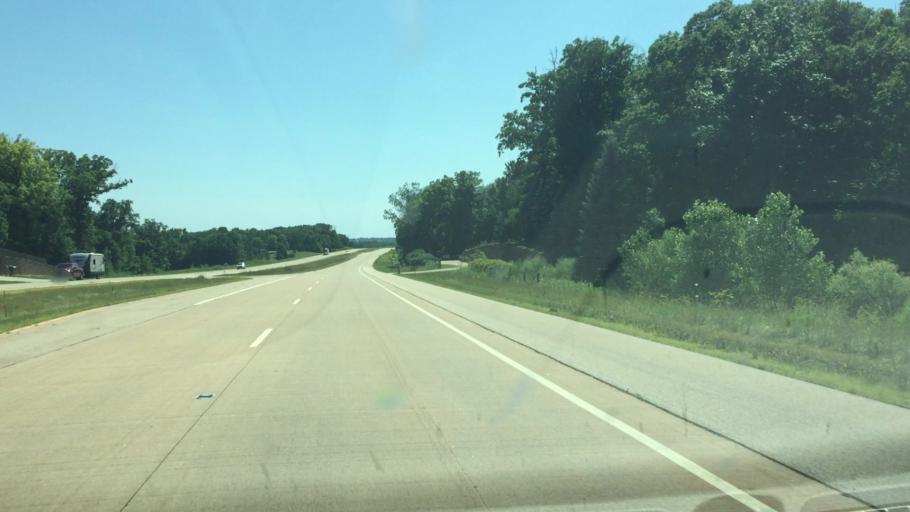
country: US
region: Wisconsin
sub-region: Grant County
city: Platteville
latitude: 42.6843
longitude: -90.5363
